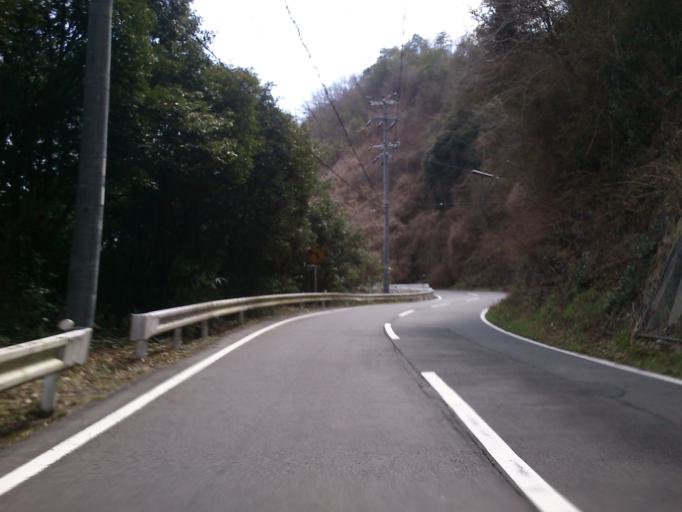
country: JP
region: Mie
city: Ueno-ebisumachi
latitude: 34.7606
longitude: 136.0087
